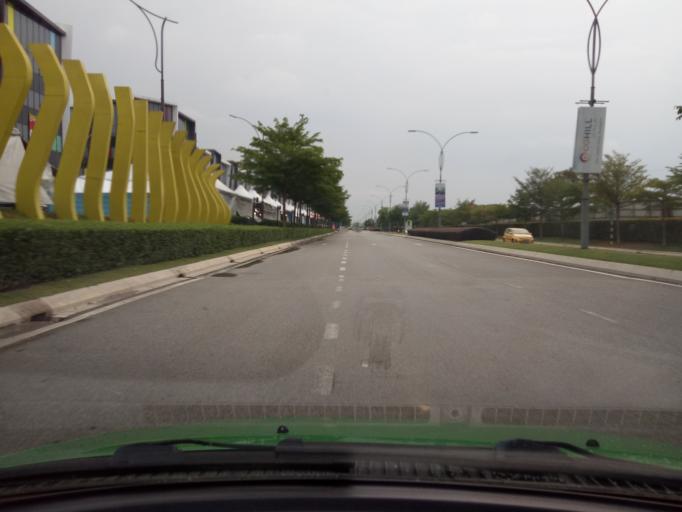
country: MY
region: Selangor
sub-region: Hulu Langat
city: Semenyih
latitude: 2.9262
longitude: 101.8580
